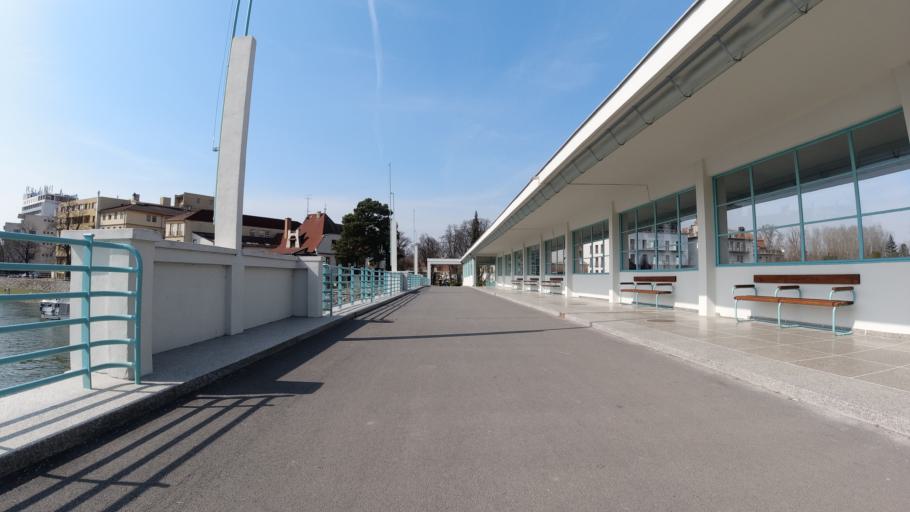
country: SK
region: Trnavsky
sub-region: Okres Trnava
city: Piestany
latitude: 48.5883
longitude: 17.8398
